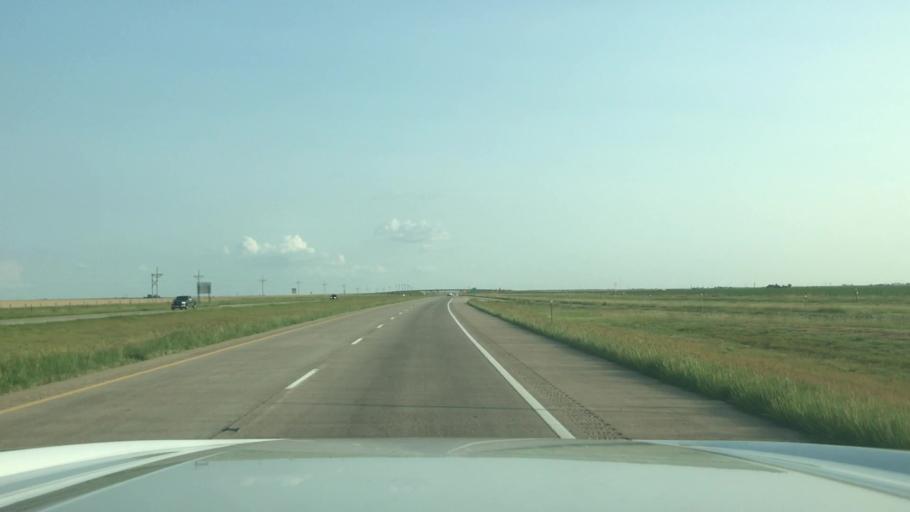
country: US
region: Texas
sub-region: Randall County
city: Canyon
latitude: 34.8508
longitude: -101.8489
